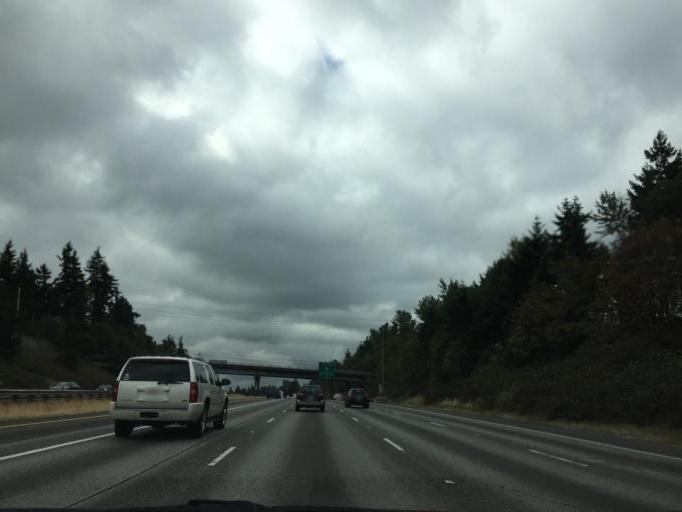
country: US
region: Washington
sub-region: King County
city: Des Moines
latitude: 47.4098
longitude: -122.2919
